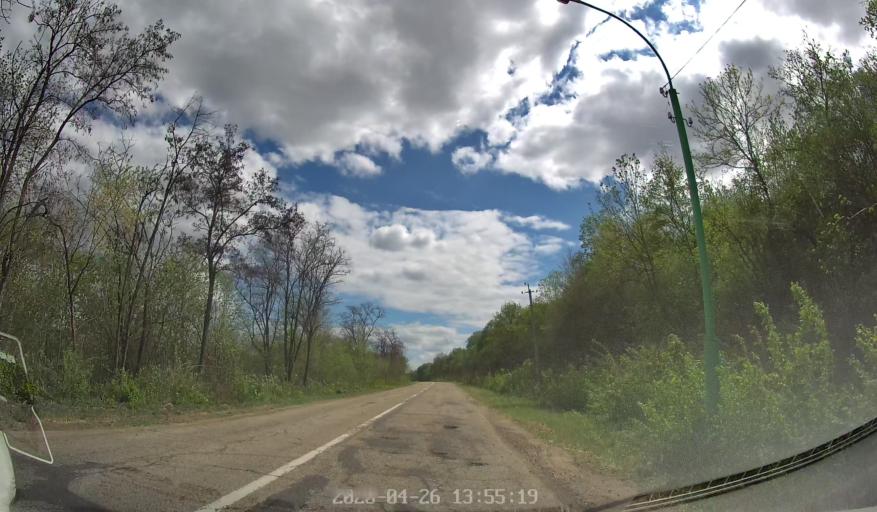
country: MD
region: Telenesti
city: Cocieri
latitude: 47.2860
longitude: 29.1006
